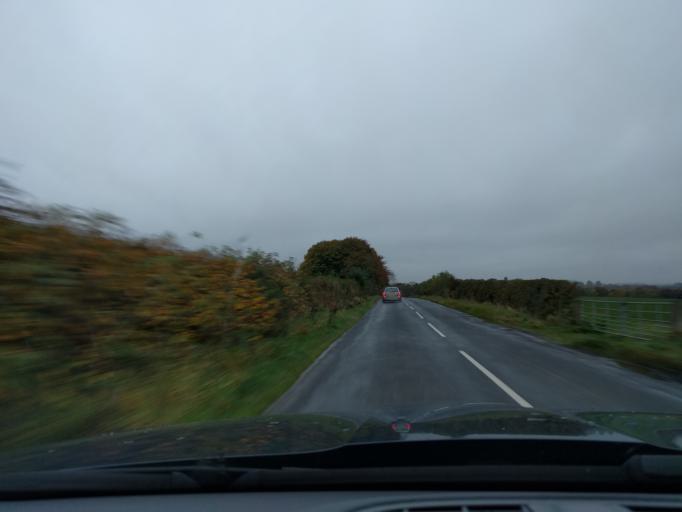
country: GB
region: Scotland
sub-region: The Scottish Borders
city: Allanton
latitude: 55.7227
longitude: -2.1391
